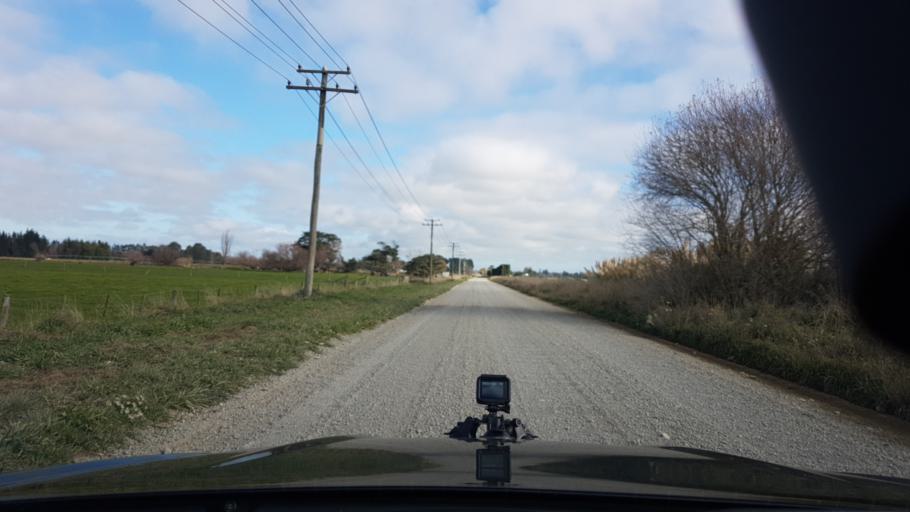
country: NZ
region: Canterbury
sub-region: Waimakariri District
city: Woodend
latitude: -43.3220
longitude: 172.6272
